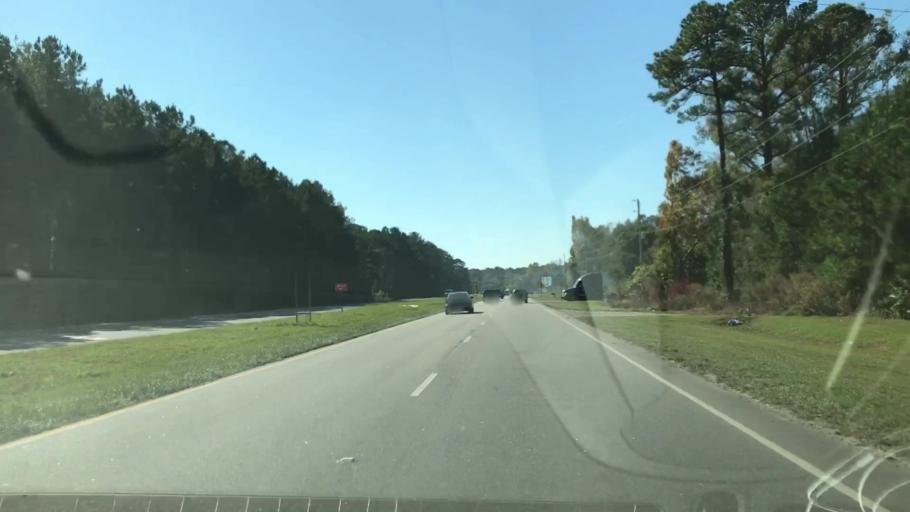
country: US
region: South Carolina
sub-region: Beaufort County
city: Bluffton
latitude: 32.3269
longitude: -80.9311
